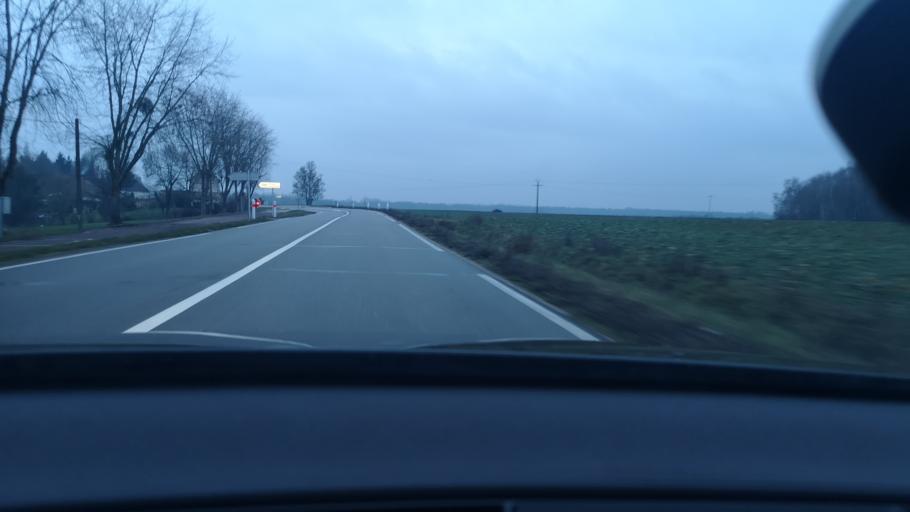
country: FR
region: Bourgogne
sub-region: Departement de la Cote-d'Or
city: Seurre
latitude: 47.0611
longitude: 5.0940
